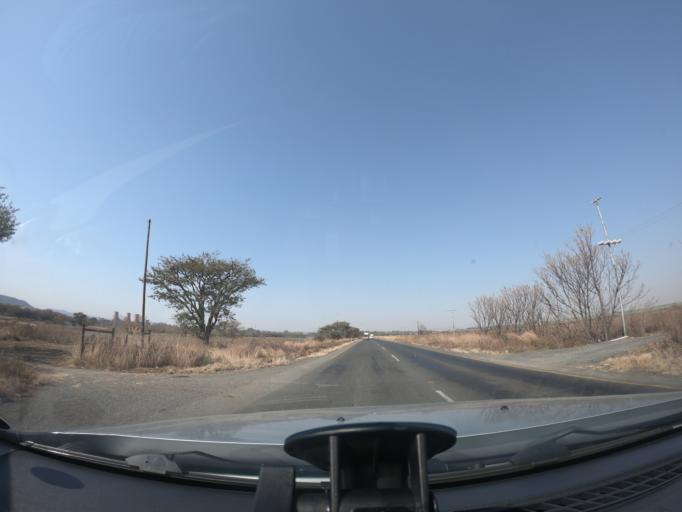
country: ZA
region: KwaZulu-Natal
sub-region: uThukela District Municipality
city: Ladysmith
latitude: -28.7311
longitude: 29.8119
